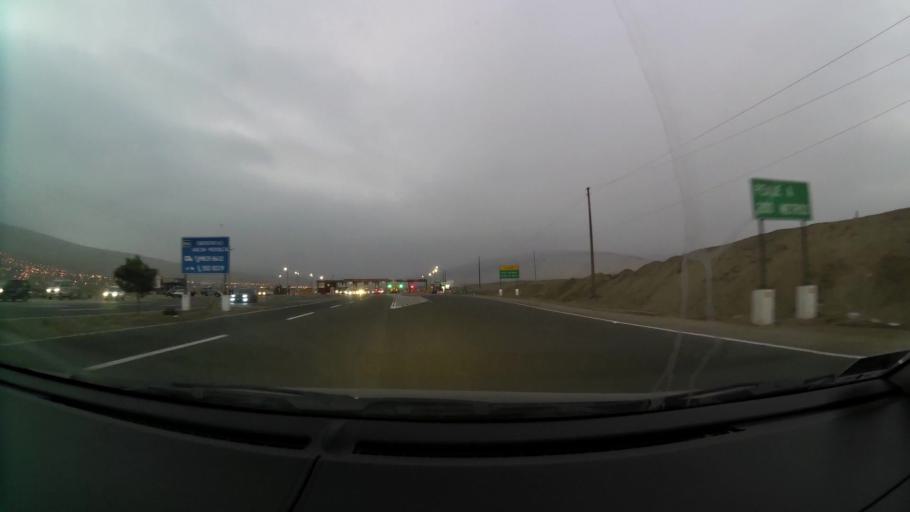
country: PE
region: Lima
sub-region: Lima
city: Santa Rosa
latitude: -11.7490
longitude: -77.1449
